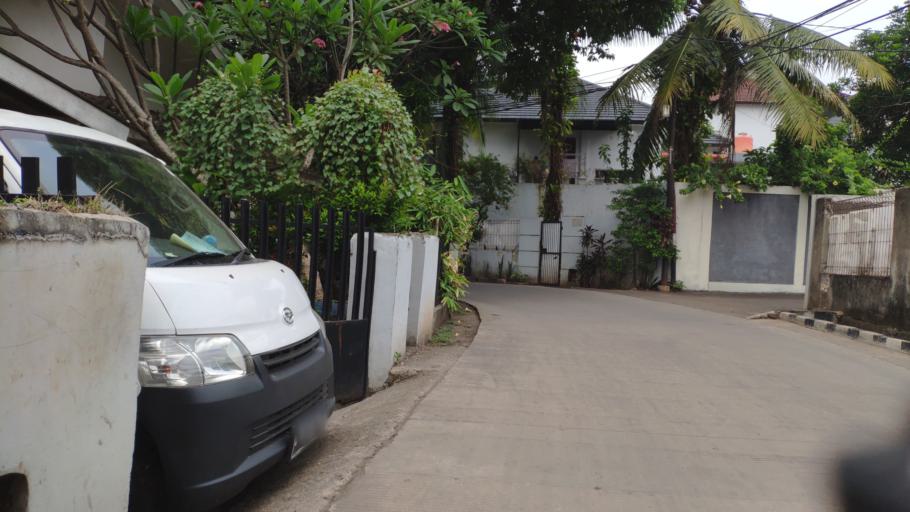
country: ID
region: West Java
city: Depok
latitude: -6.3135
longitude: 106.8305
